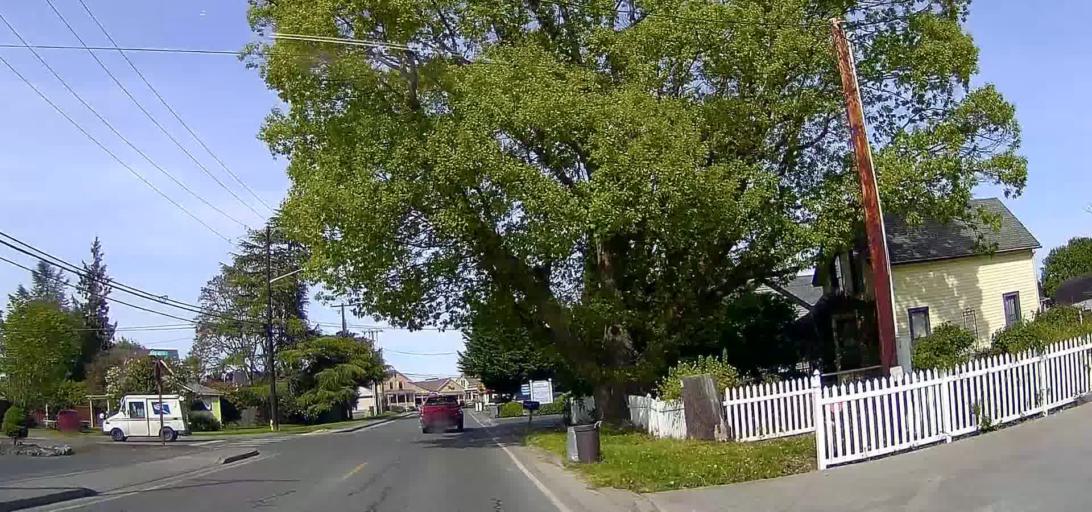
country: US
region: Washington
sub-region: Skagit County
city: Mount Vernon
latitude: 48.3909
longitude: -122.4901
